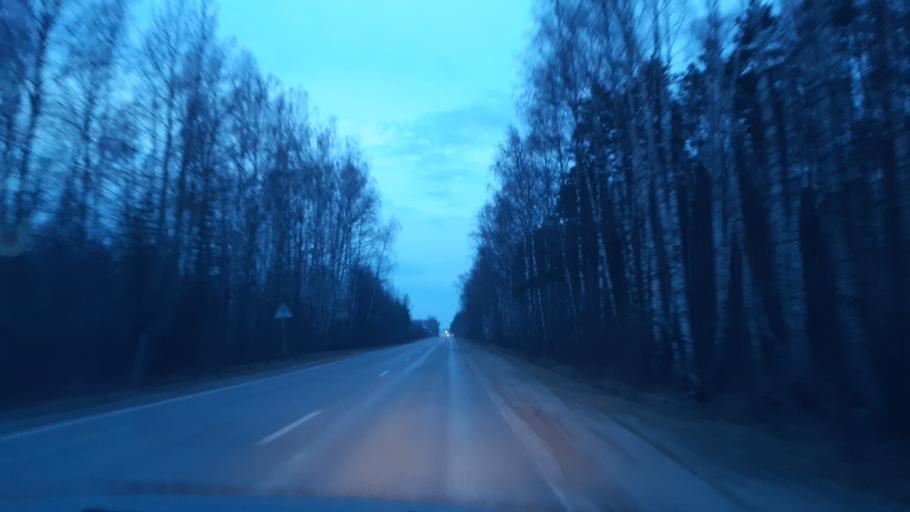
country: RU
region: Vladimir
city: Luknovo
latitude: 56.2266
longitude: 42.0348
